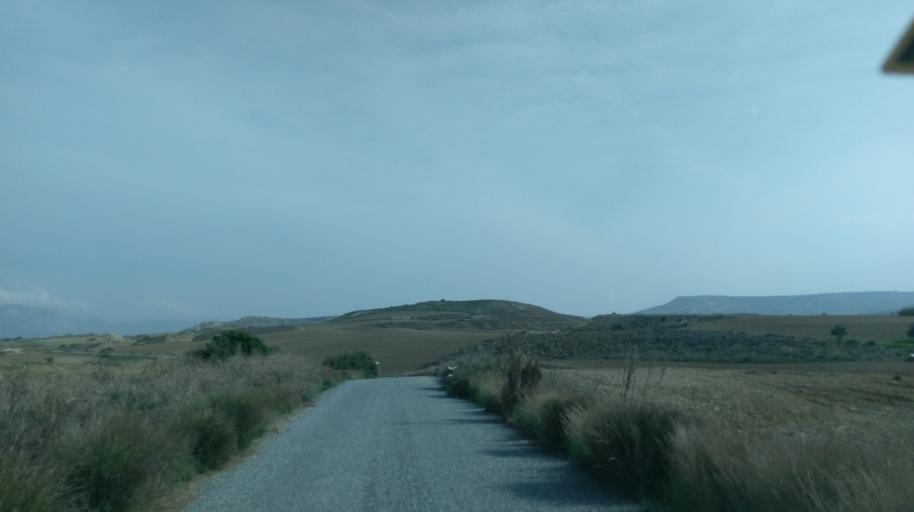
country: CY
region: Lefkosia
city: Morfou
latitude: 35.2514
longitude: 33.0742
